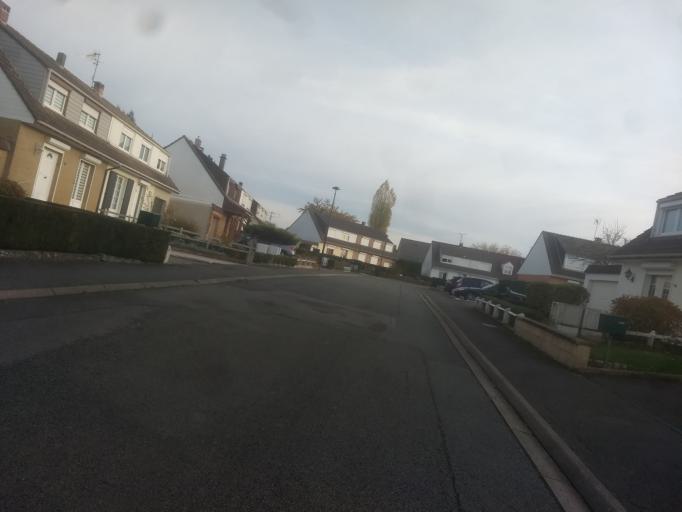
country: FR
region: Nord-Pas-de-Calais
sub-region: Departement du Pas-de-Calais
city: Beaurains
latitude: 50.2694
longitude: 2.7800
